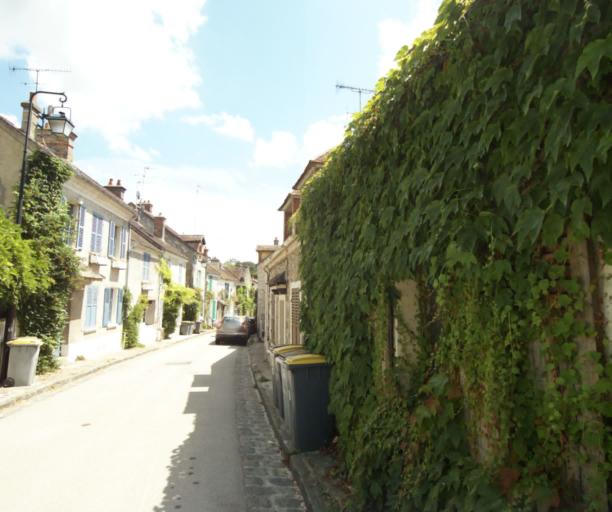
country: FR
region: Ile-de-France
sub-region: Departement de Seine-et-Marne
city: Samois-sur-Seine
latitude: 48.4513
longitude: 2.7558
